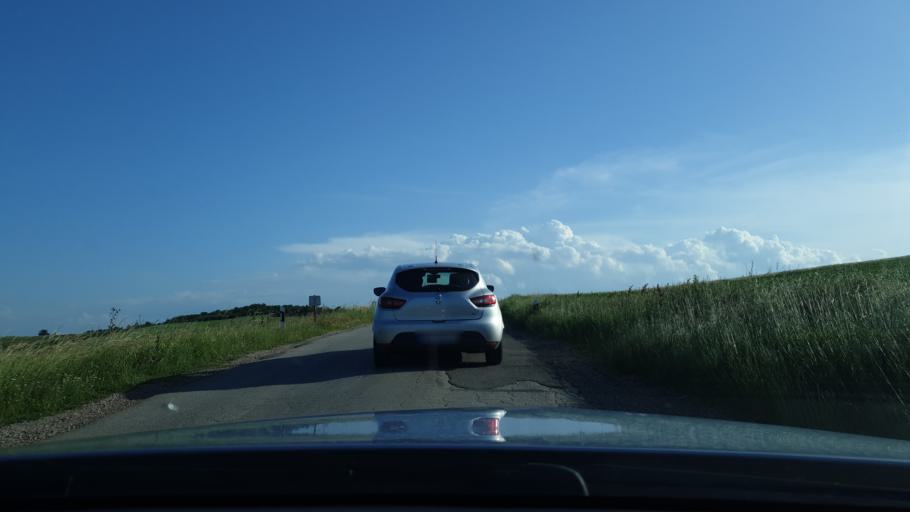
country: RS
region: Central Serbia
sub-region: Nisavski Okrug
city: Aleksinac
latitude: 43.6210
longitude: 21.6781
